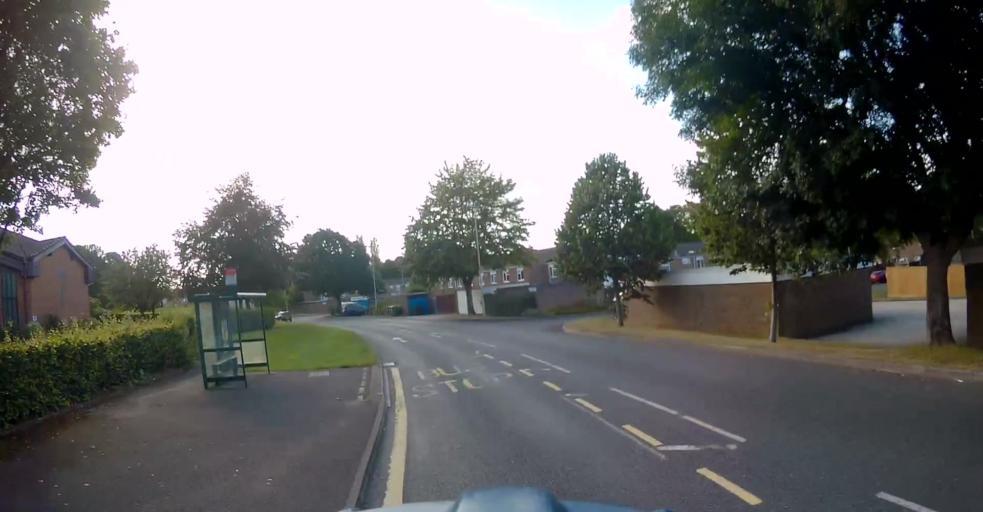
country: GB
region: England
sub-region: Hampshire
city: Basingstoke
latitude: 51.2452
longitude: -1.1207
